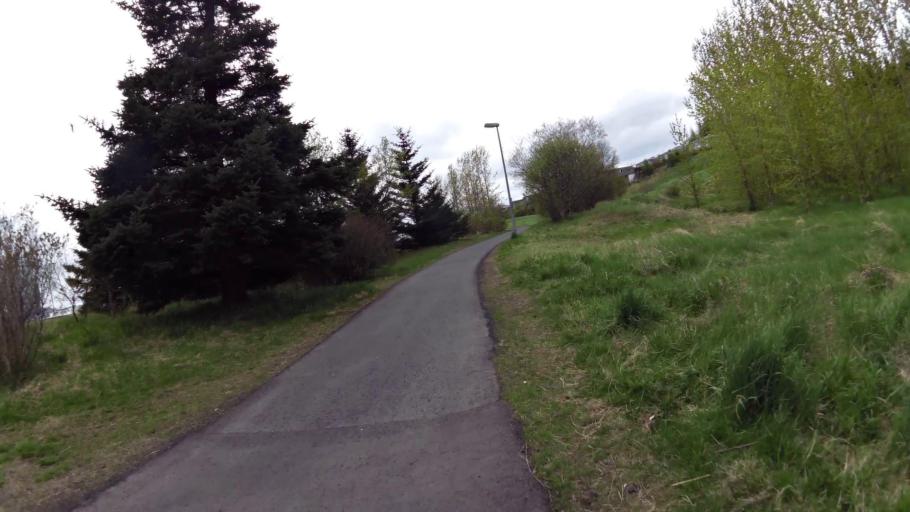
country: IS
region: Capital Region
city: Reykjavik
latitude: 64.1062
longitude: -21.8730
